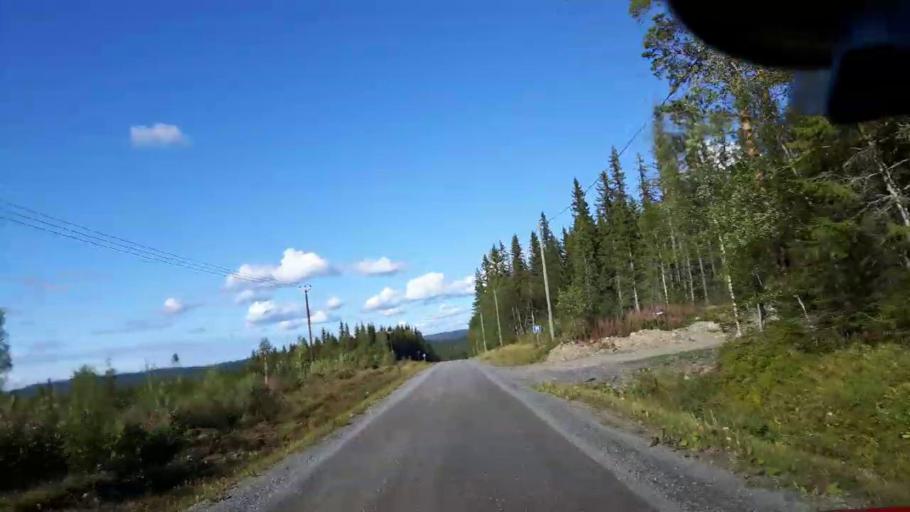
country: SE
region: Jaemtland
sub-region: Ragunda Kommun
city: Hammarstrand
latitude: 63.5076
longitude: 16.0426
